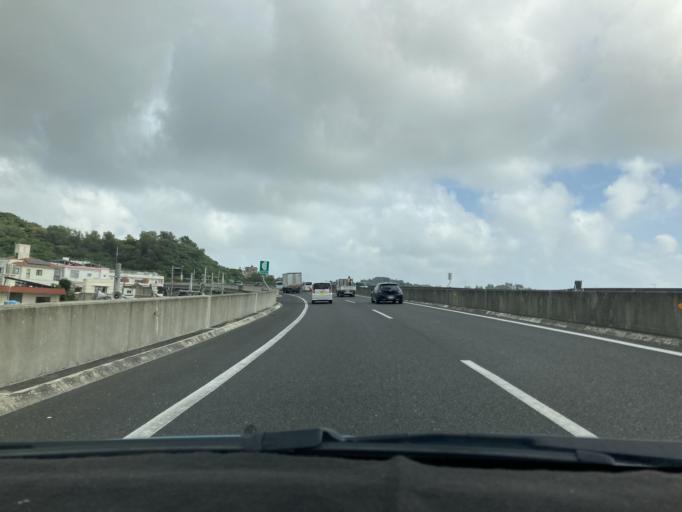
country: JP
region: Okinawa
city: Tomigusuku
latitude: 26.1728
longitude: 127.6764
